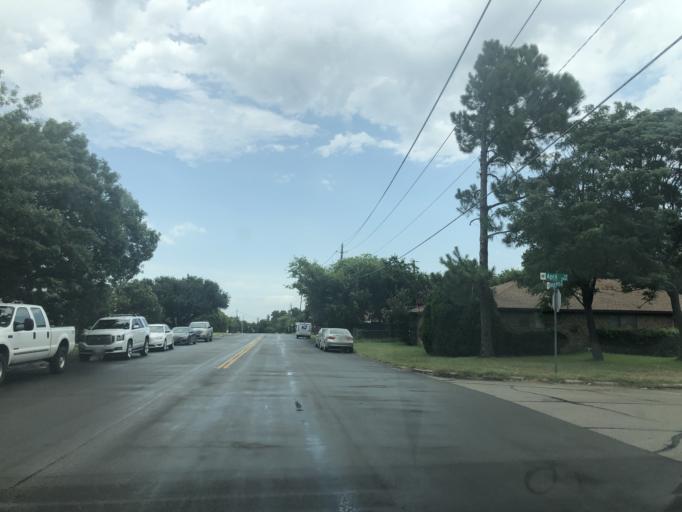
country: US
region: Texas
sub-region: Dallas County
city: Grand Prairie
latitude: 32.7480
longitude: -97.0401
